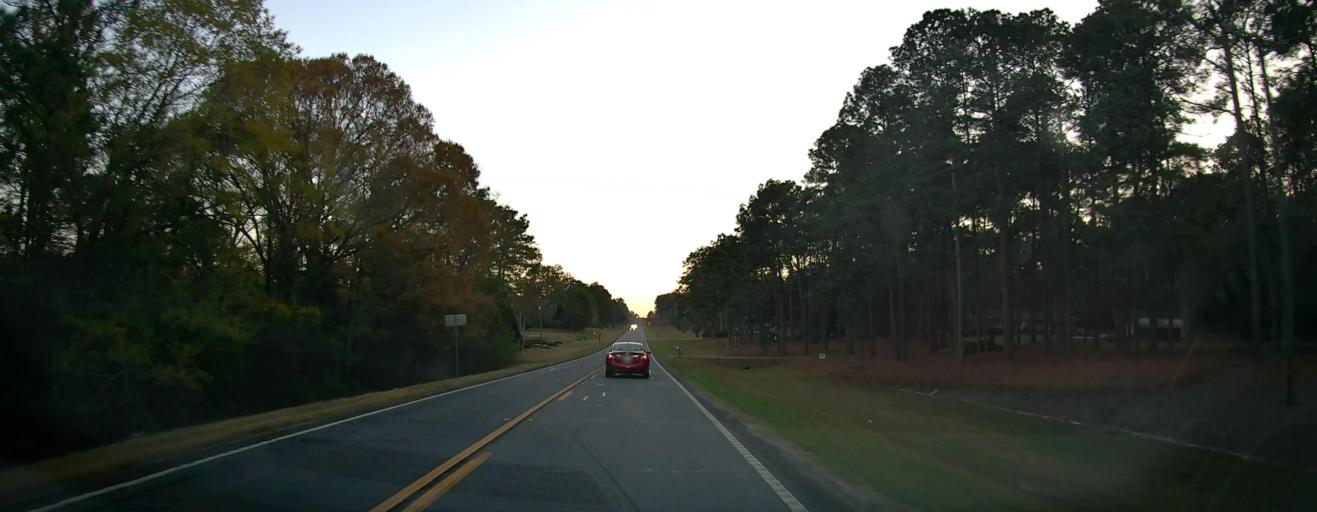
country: US
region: Georgia
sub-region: Dodge County
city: Eastman
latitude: 32.2216
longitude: -83.1563
